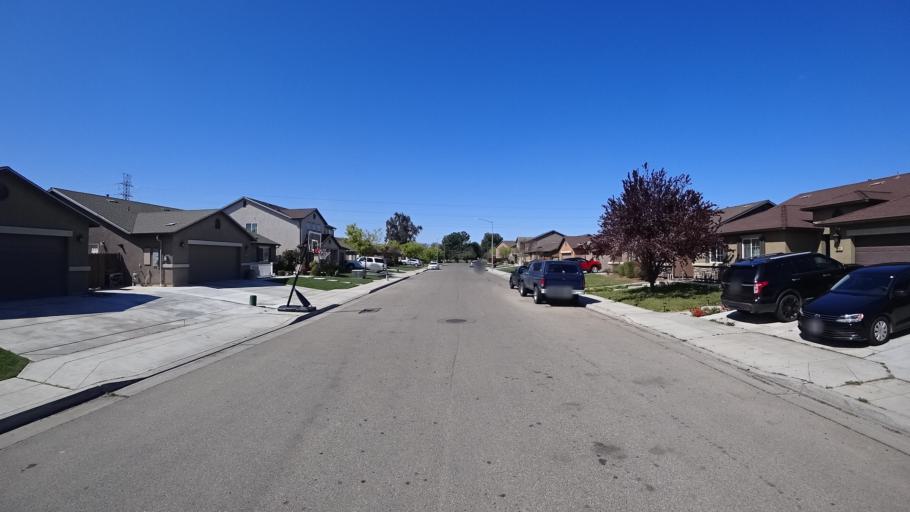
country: US
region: California
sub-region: Fresno County
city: West Park
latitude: 36.7850
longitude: -119.8963
